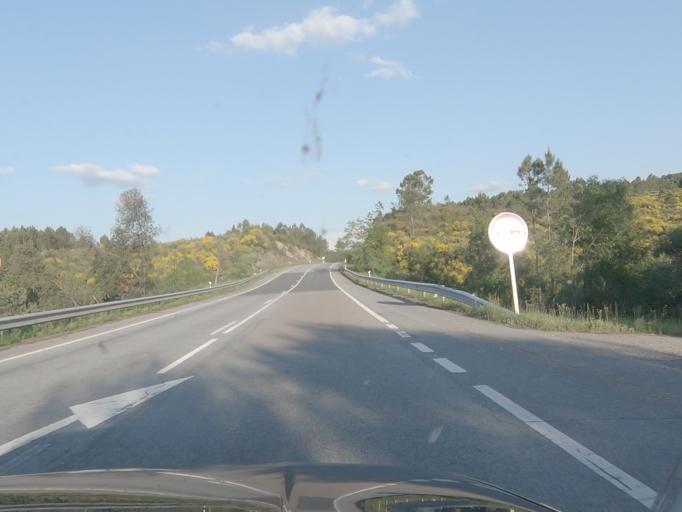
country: PT
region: Portalegre
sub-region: Marvao
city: Marvao
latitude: 39.3721
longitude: -7.3514
